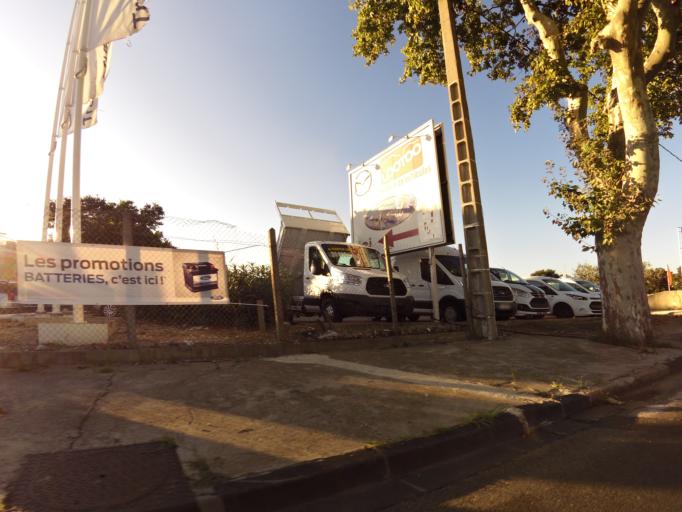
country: FR
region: Languedoc-Roussillon
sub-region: Departement du Gard
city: Nimes
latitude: 43.8162
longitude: 4.3371
